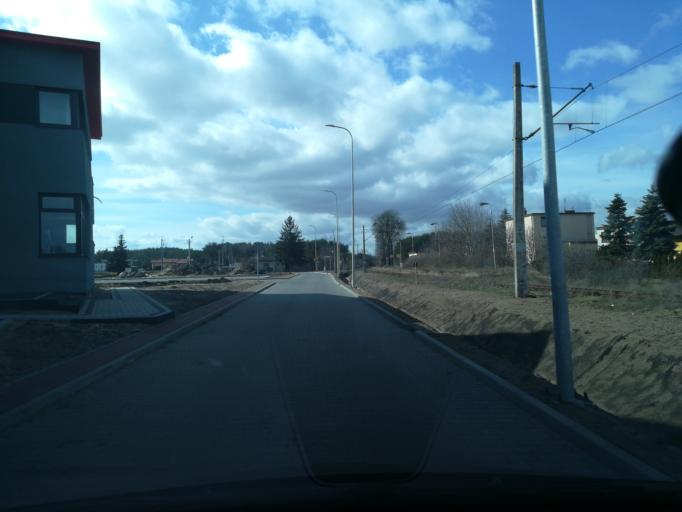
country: PL
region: Kujawsko-Pomorskie
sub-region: Powiat aleksandrowski
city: Ciechocinek
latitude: 52.8701
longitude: 18.7491
